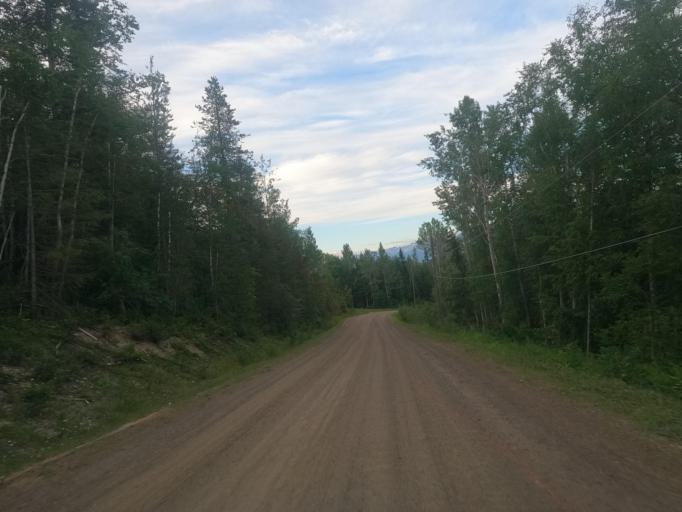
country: CA
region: British Columbia
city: Golden
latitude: 51.4524
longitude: -117.0038
